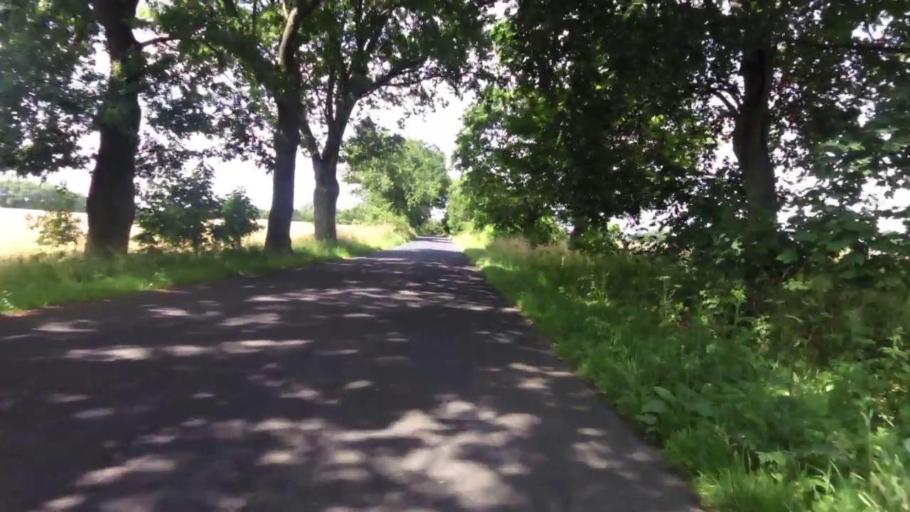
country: PL
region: West Pomeranian Voivodeship
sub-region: Powiat stargardzki
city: Dobrzany
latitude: 53.4283
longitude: 15.4616
